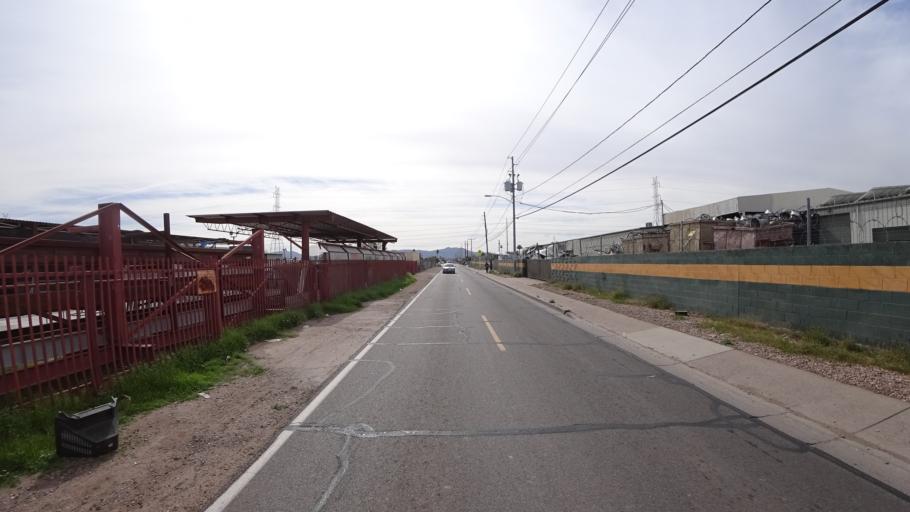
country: US
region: Arizona
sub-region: Maricopa County
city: Phoenix
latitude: 33.4416
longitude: -112.1260
